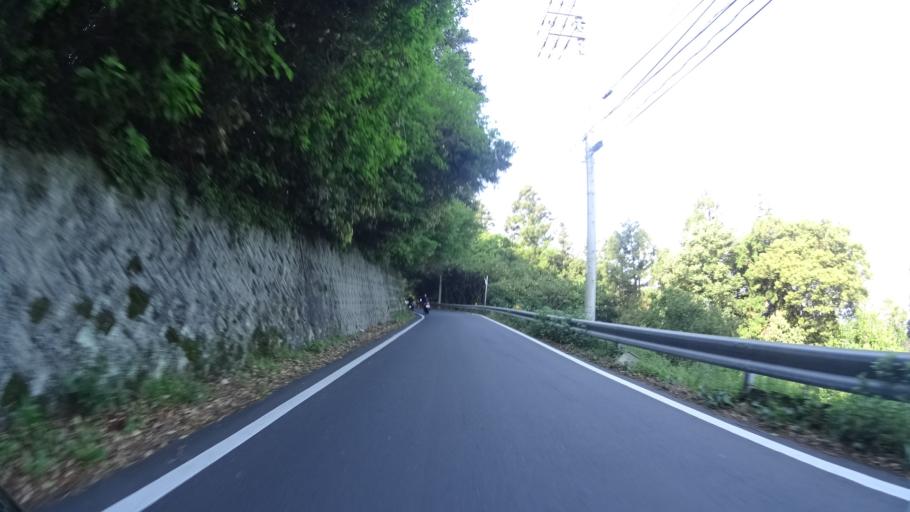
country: JP
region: Ehime
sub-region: Nishiuwa-gun
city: Ikata-cho
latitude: 33.3790
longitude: 132.0655
